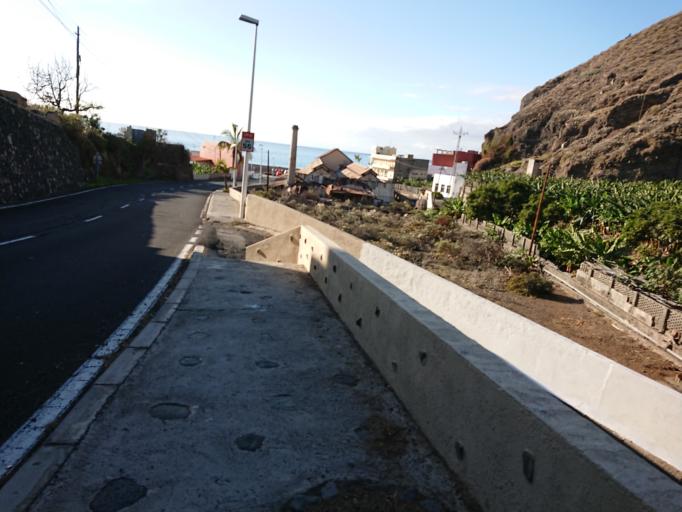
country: ES
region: Canary Islands
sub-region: Provincia de Santa Cruz de Tenerife
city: Tazacorte
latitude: 28.6474
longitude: -17.9421
